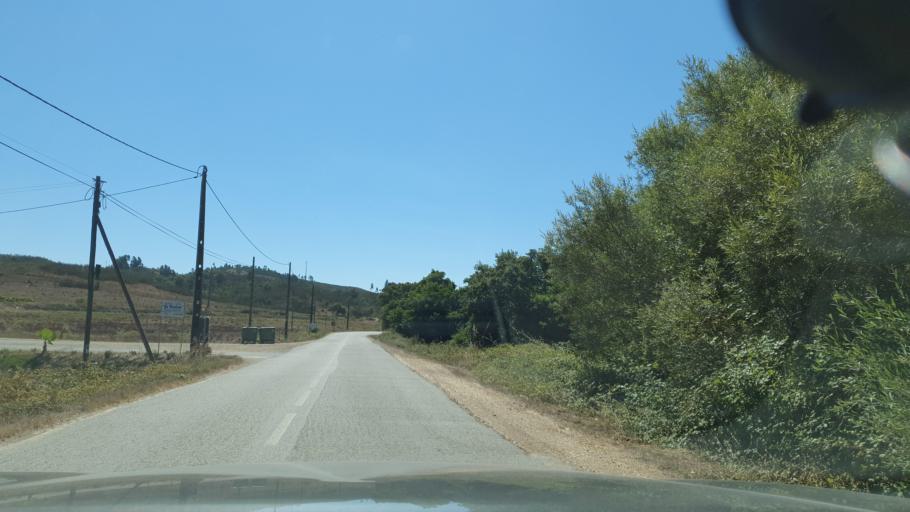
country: PT
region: Beja
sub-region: Odemira
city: Sao Teotonio
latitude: 37.4869
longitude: -8.6366
